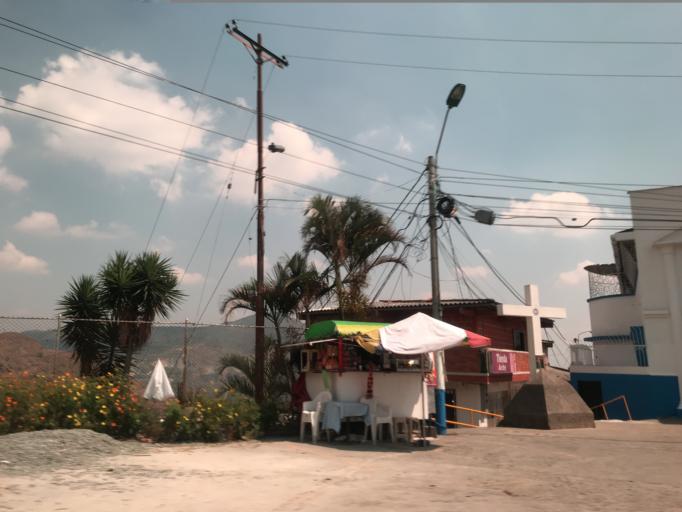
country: CO
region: Valle del Cauca
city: Cali
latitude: 3.4535
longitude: -76.5704
